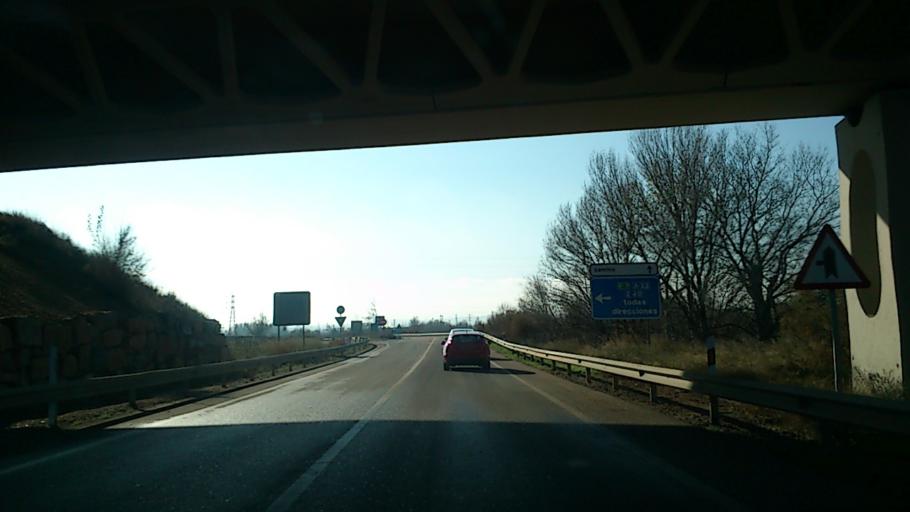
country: ES
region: Aragon
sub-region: Provincia de Zaragoza
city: Zaragoza
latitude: 41.6939
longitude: -0.8355
